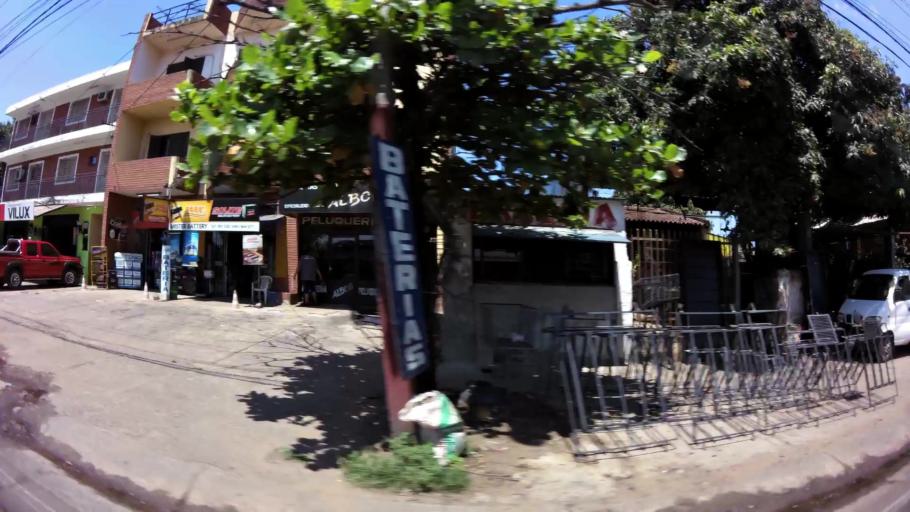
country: PY
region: Central
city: Lambare
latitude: -25.3319
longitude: -57.5753
